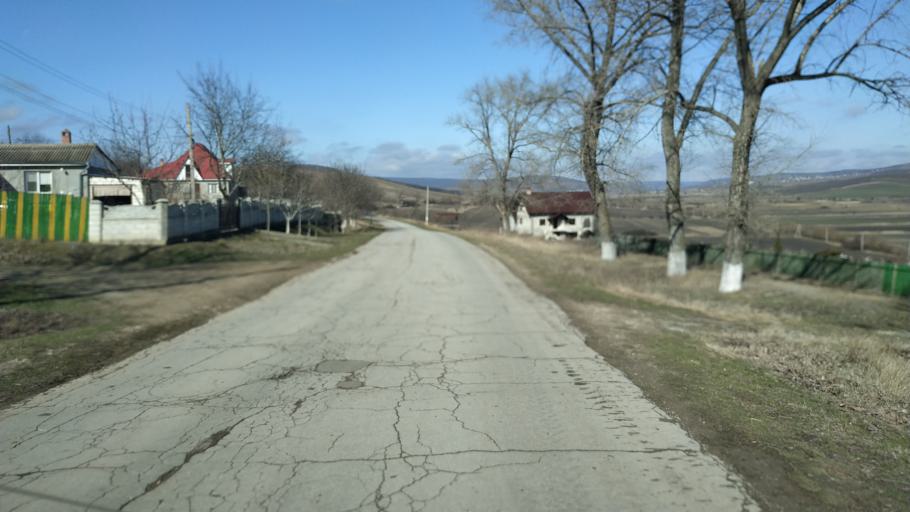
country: MD
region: Hincesti
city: Hincesti
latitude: 46.9757
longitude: 28.5749
